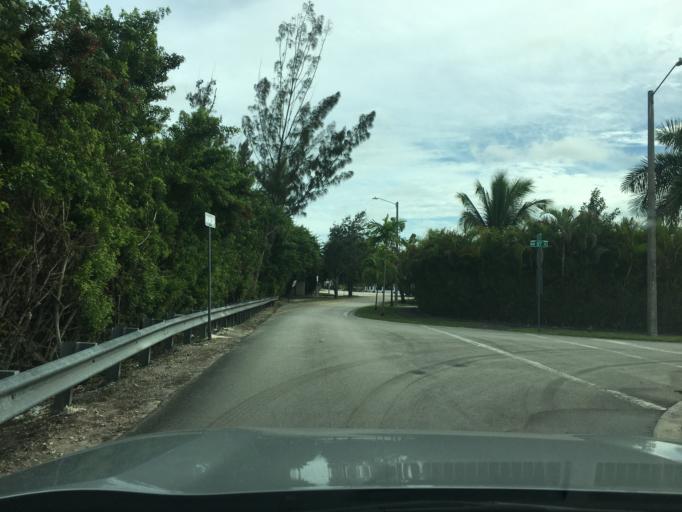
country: US
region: Florida
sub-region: Miami-Dade County
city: Palm Springs North
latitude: 25.9380
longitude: -80.3435
